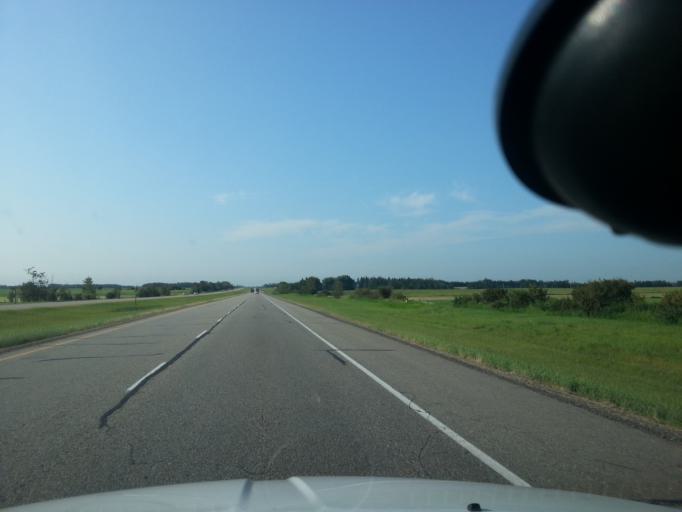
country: CA
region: Alberta
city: Millet
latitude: 52.9956
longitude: -113.6437
